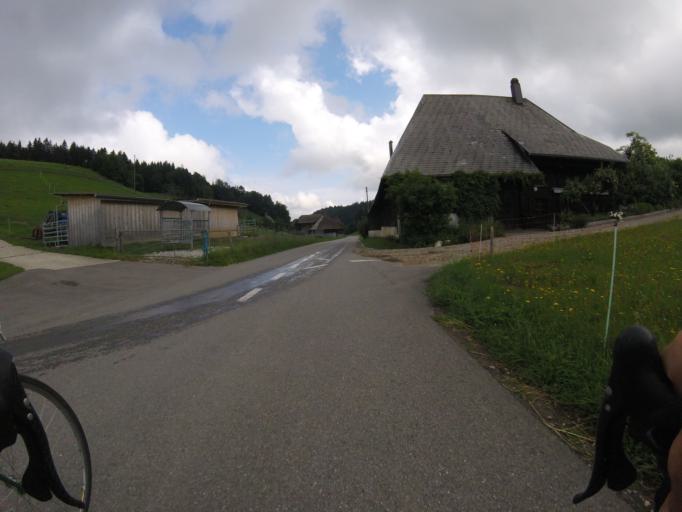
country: CH
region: Bern
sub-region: Emmental District
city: Krauchthal
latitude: 46.9794
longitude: 7.5809
